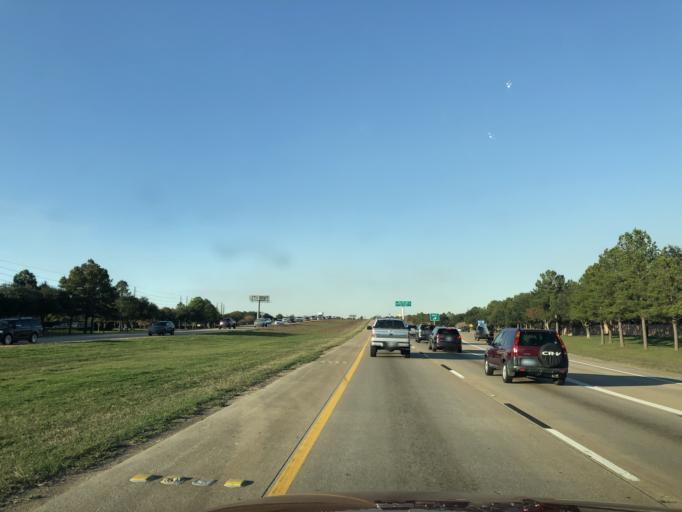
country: US
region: Texas
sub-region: Fort Bend County
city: Cinco Ranch
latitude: 29.7399
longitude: -95.7728
